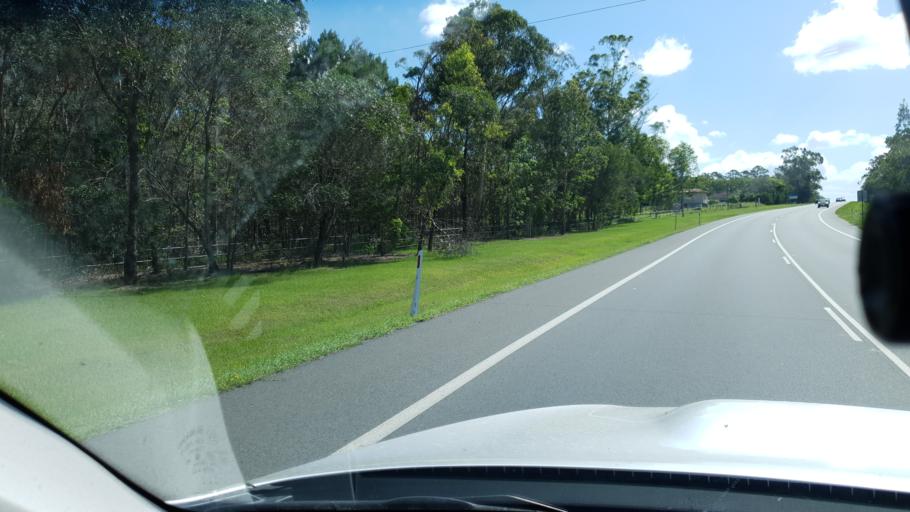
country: AU
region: Queensland
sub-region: Logan
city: Woodridge
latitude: -27.6496
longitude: 153.0844
